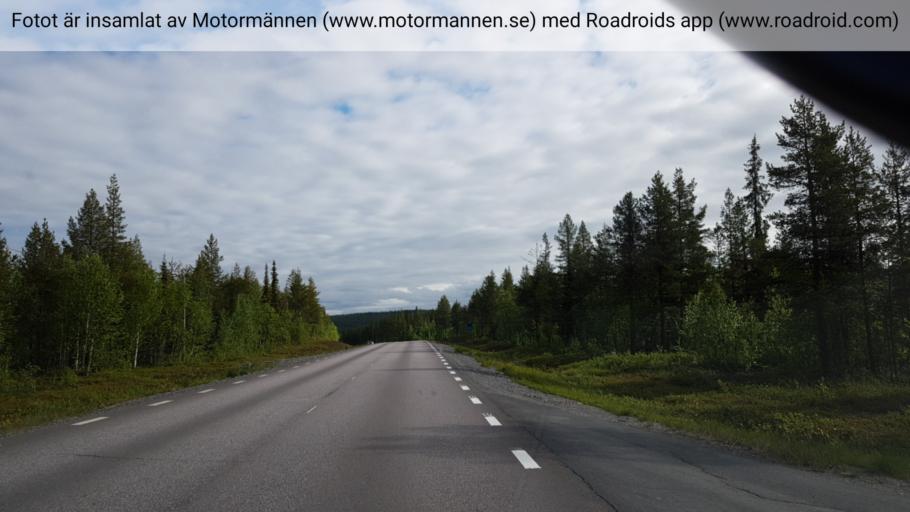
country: SE
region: Norrbotten
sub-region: Gallivare Kommun
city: Malmberget
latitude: 67.4703
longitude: 21.1262
